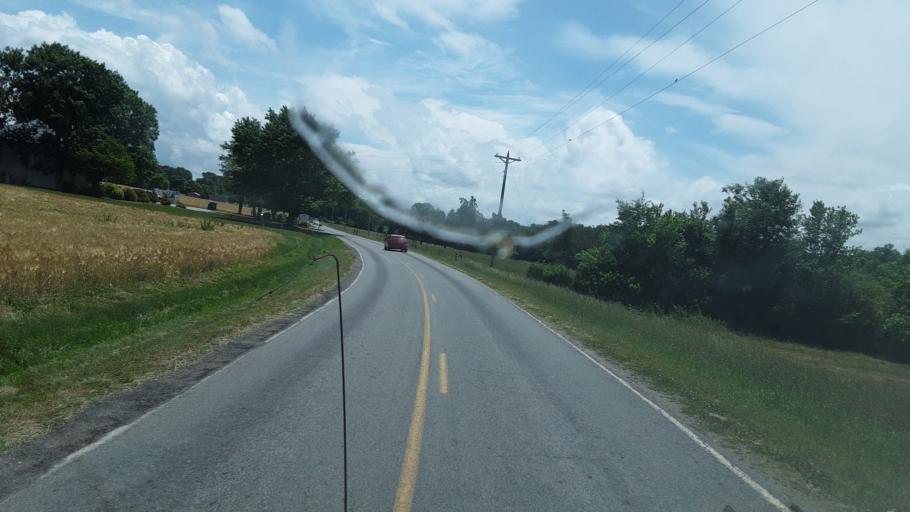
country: US
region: North Carolina
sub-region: Yadkin County
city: Jonesville
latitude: 36.0943
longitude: -80.8648
